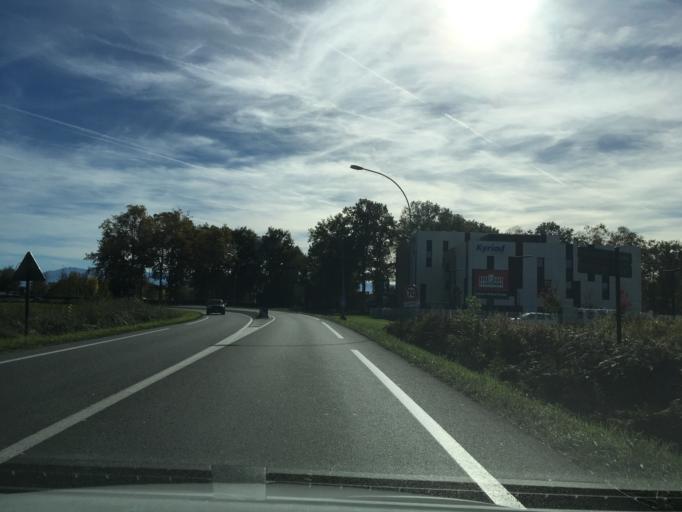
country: FR
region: Aquitaine
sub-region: Departement des Pyrenees-Atlantiques
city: Pau
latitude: 43.3327
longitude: -0.3583
